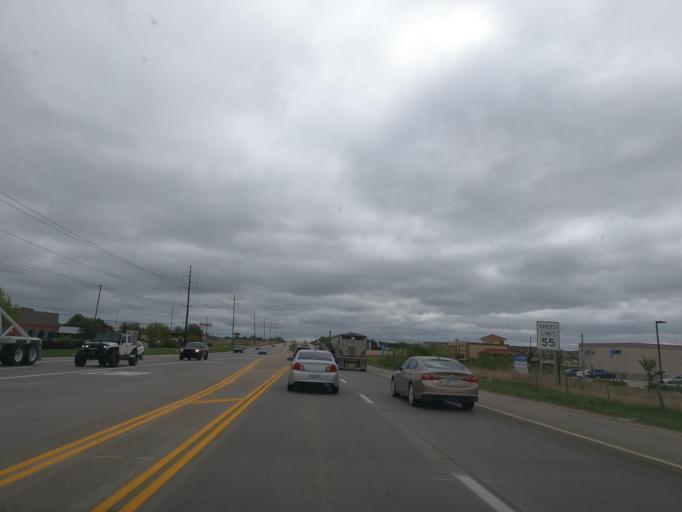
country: US
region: Kansas
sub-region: Butler County
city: Andover
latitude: 37.6795
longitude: -97.1341
